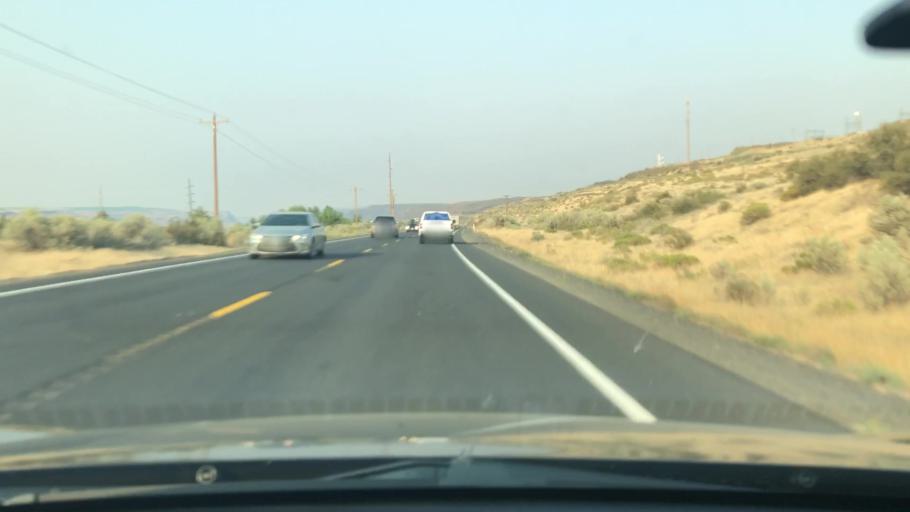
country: US
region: Oregon
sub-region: Umatilla County
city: Stanfield
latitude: 45.9201
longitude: -119.1235
